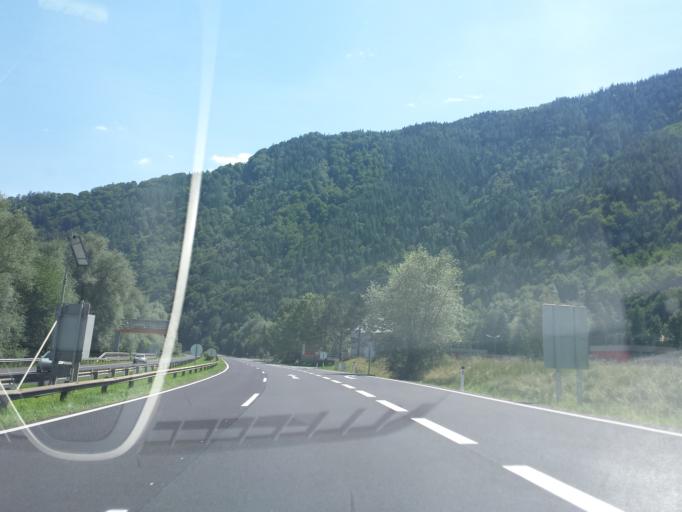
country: AT
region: Styria
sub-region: Politischer Bezirk Bruck-Muerzzuschlag
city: Bruck an der Mur
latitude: 47.3959
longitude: 15.2853
